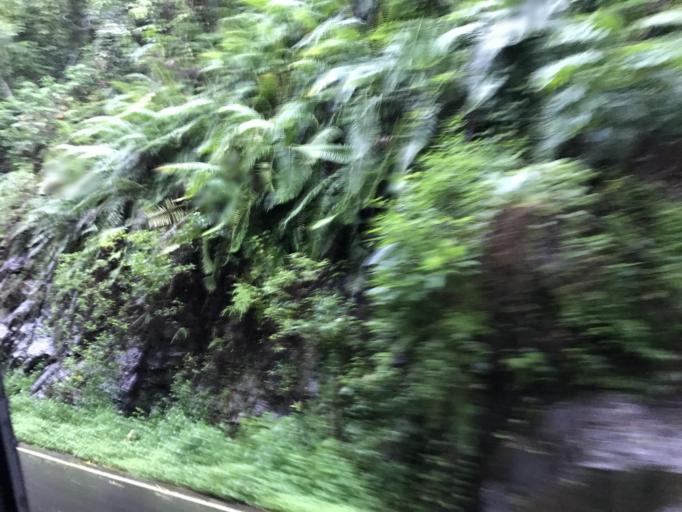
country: LK
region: Sabaragamuwa
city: Ratnapura
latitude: 6.5395
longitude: 80.3036
